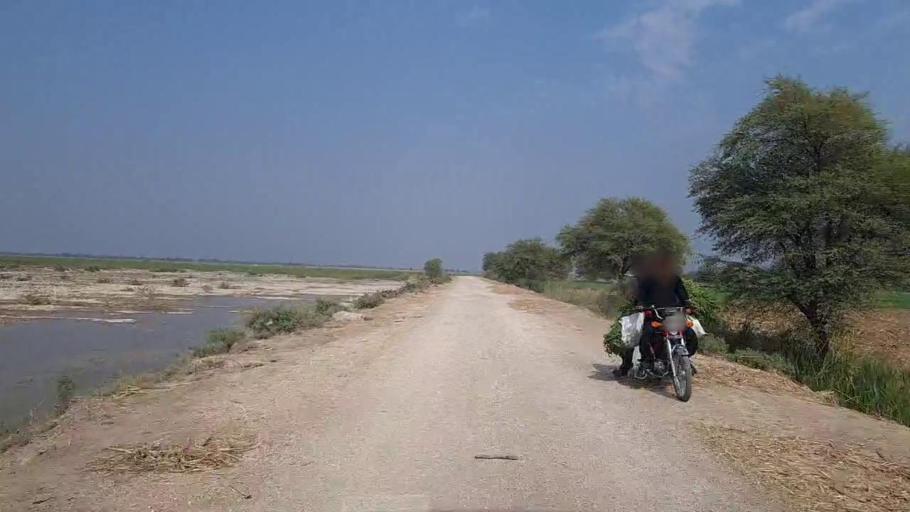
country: PK
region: Sindh
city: Mirwah Gorchani
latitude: 25.3752
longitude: 69.0399
